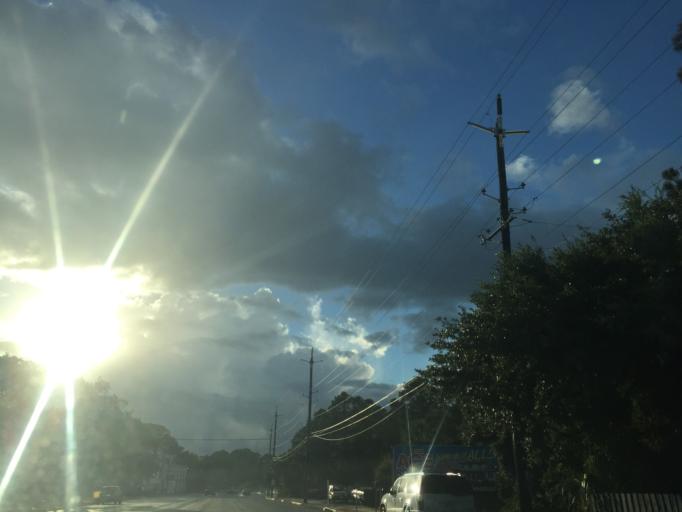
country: US
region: Georgia
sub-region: Chatham County
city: Tybee Island
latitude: 32.0134
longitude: -80.8442
